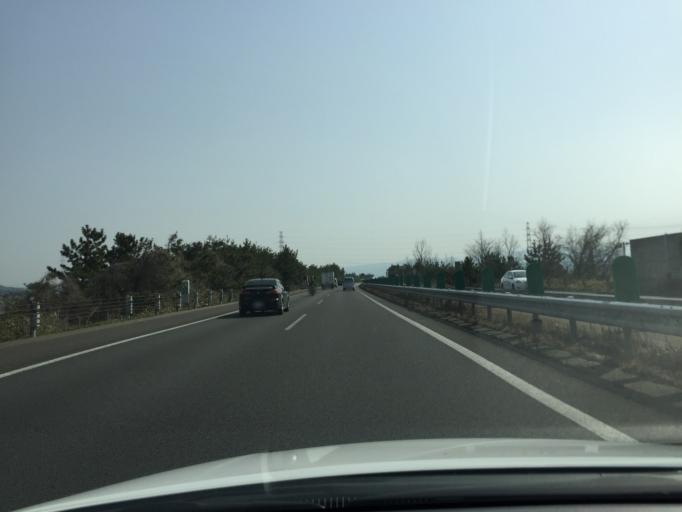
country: JP
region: Fukushima
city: Fukushima-shi
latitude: 37.8010
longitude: 140.4428
